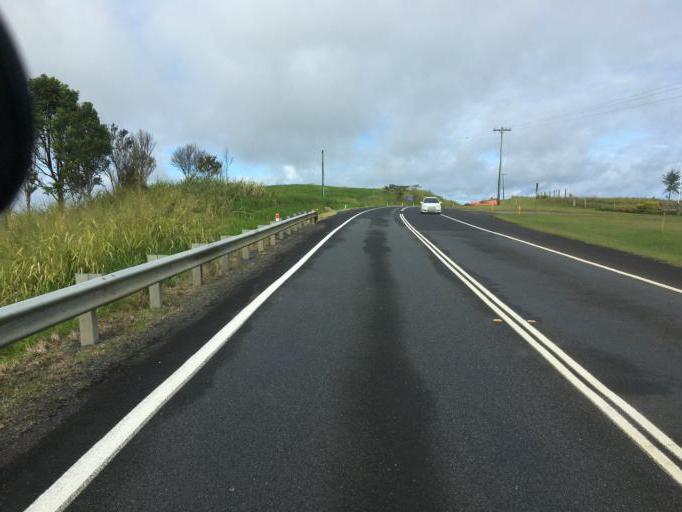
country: AU
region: Queensland
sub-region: Tablelands
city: Ravenshoe
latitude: -17.5355
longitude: 145.6633
